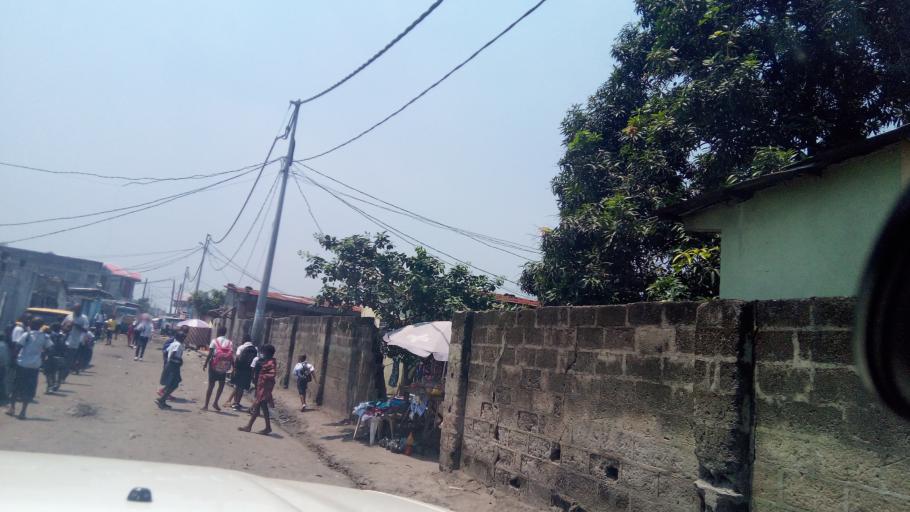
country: CD
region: Kinshasa
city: Kinshasa
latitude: -4.3707
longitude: 15.3131
